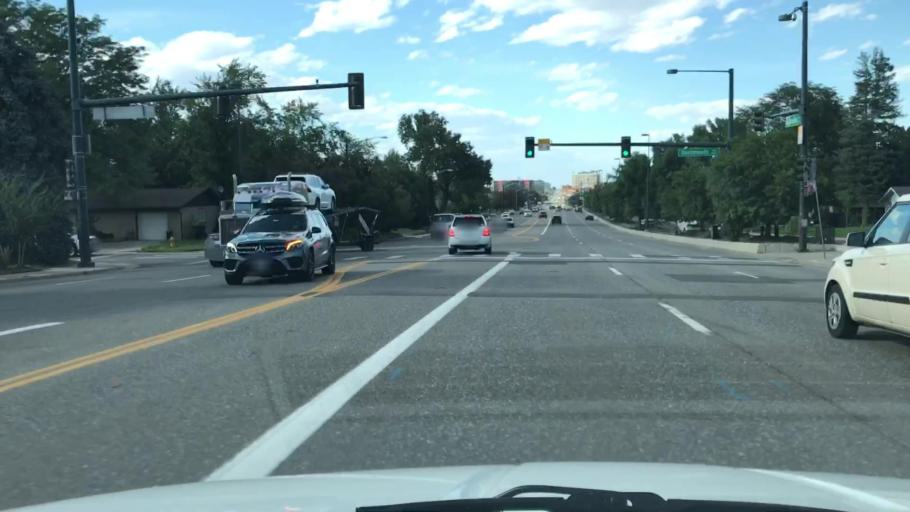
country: US
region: Colorado
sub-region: Arapahoe County
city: Cherry Hills Village
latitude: 39.6604
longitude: -104.9407
